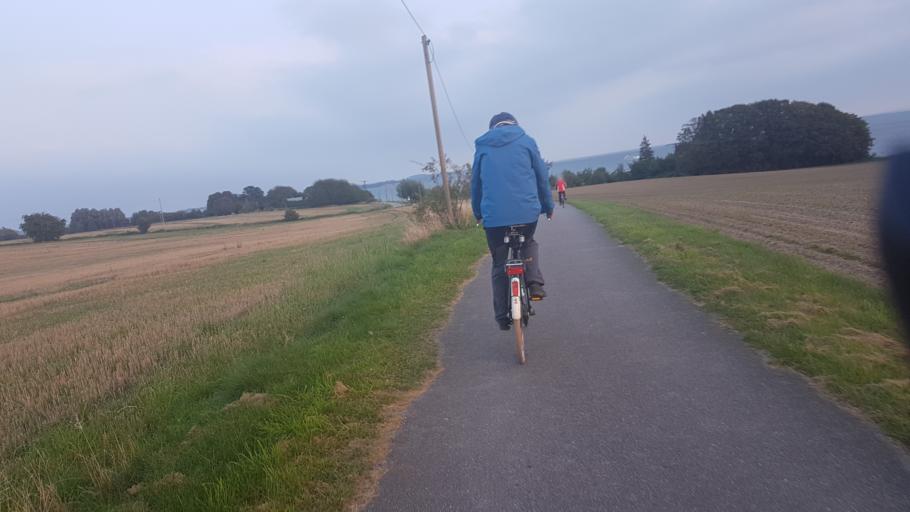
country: DE
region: Mecklenburg-Vorpommern
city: Putbus
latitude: 54.3429
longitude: 13.5473
